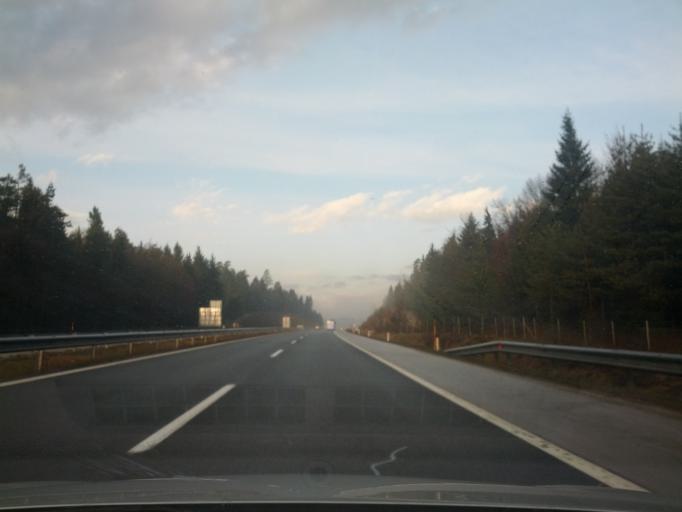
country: SI
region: Naklo
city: Naklo
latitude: 46.2685
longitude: 14.3336
